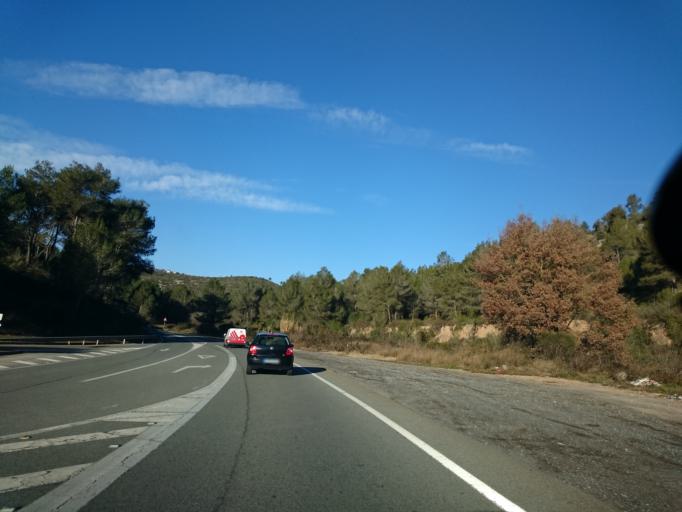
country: ES
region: Catalonia
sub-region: Provincia de Barcelona
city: Sant Pere de Ribes
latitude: 41.2871
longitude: 1.7419
